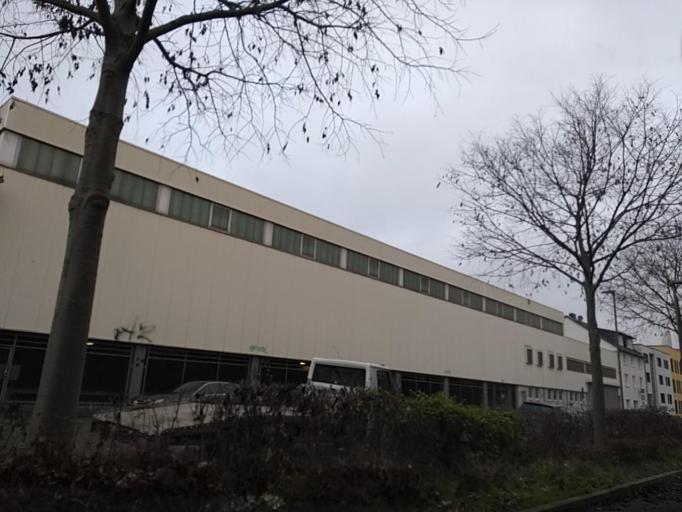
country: DE
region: Hesse
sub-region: Regierungsbezirk Kassel
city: Kassel
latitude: 51.3212
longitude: 9.4958
